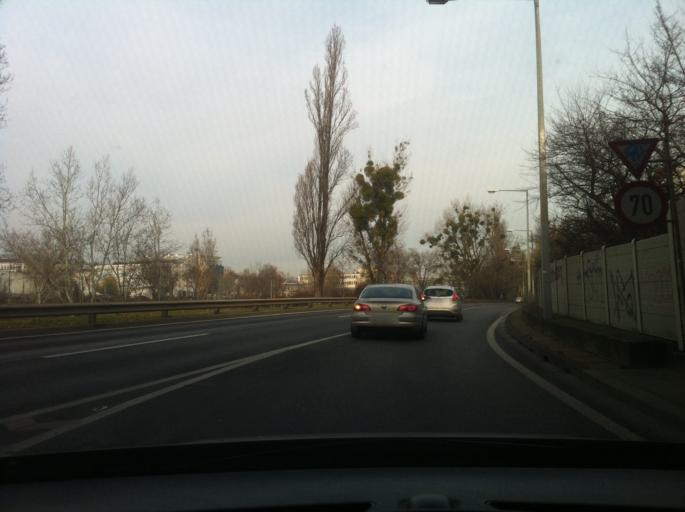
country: AT
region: Vienna
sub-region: Wien Stadt
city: Vienna
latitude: 48.2365
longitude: 16.3628
